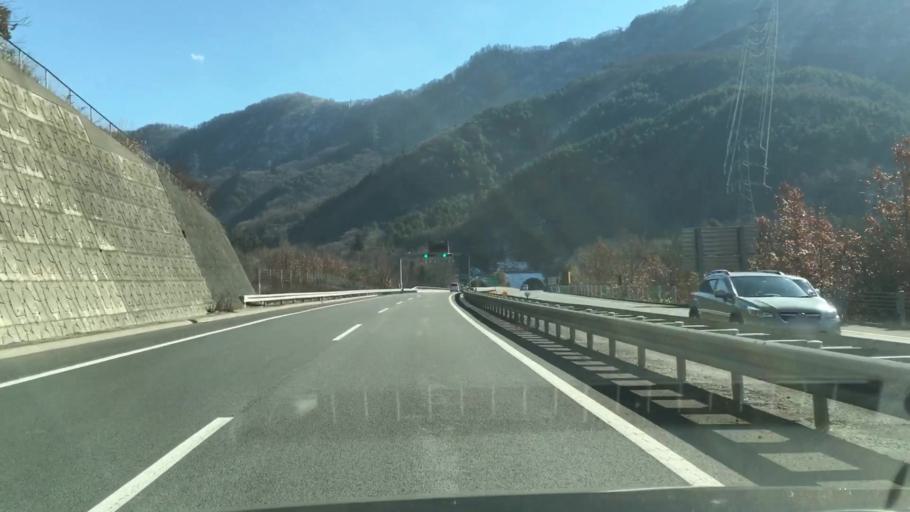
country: JP
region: Nagano
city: Ueda
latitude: 36.4421
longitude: 138.2160
